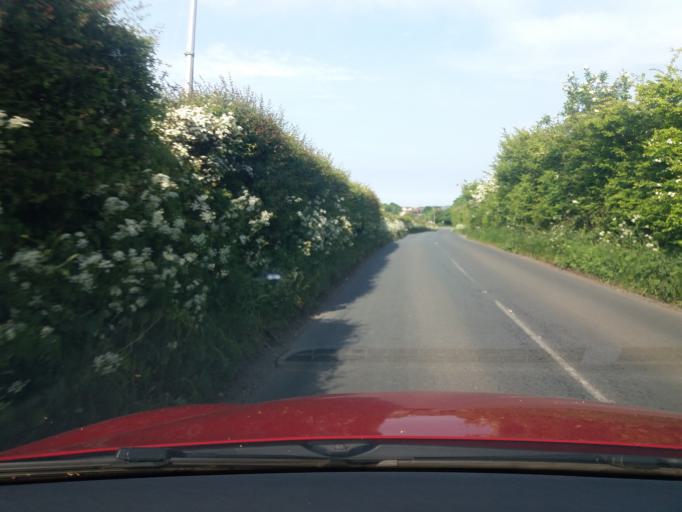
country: GB
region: England
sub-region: Lancashire
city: Chorley
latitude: 53.6889
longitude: -2.5785
